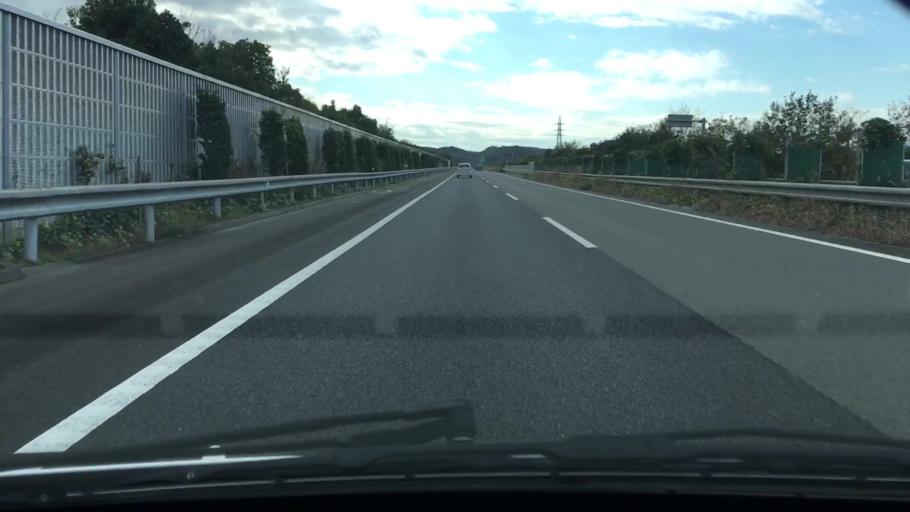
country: JP
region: Chiba
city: Kisarazu
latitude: 35.4017
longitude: 140.0070
